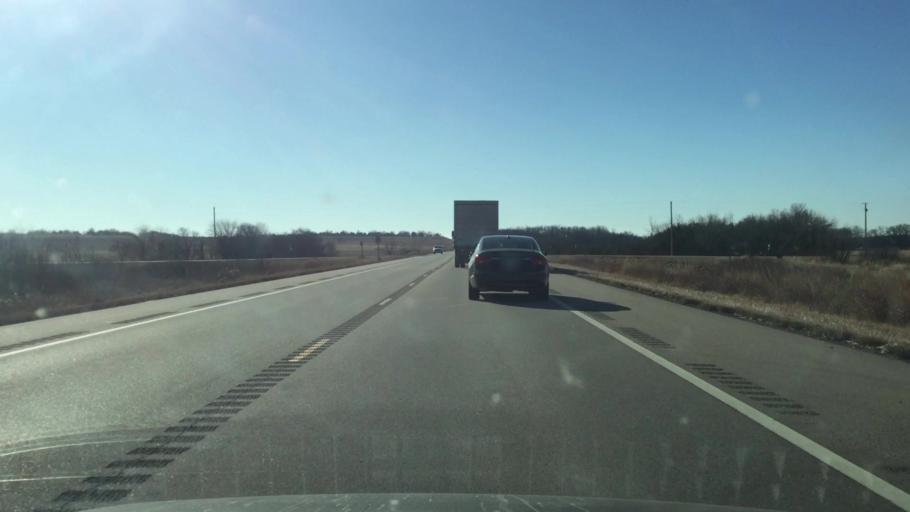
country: US
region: Kansas
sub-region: Allen County
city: Iola
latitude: 38.0257
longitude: -95.3810
